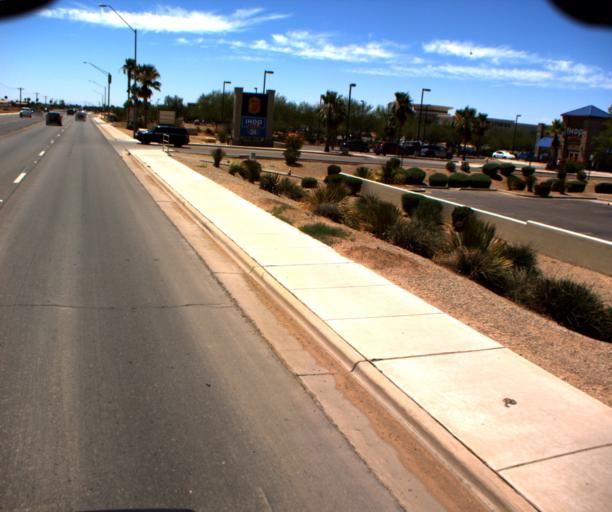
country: US
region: Arizona
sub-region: Pinal County
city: Casa Grande
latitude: 32.8797
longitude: -111.6977
